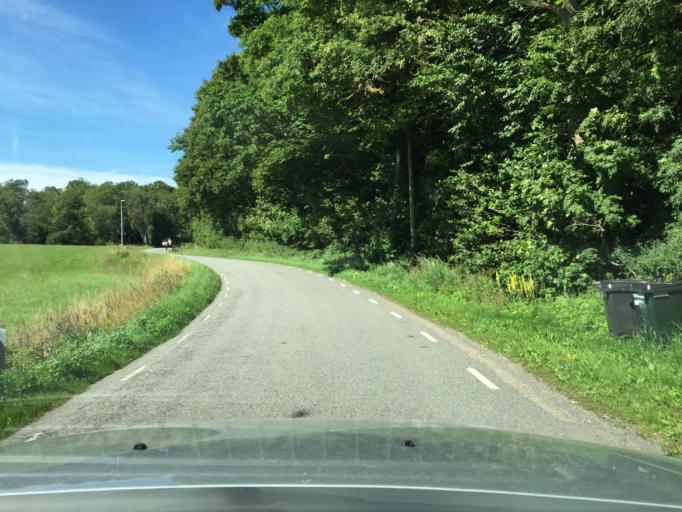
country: SE
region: Skane
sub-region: Hassleholms Kommun
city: Sosdala
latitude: 56.0409
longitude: 13.6603
